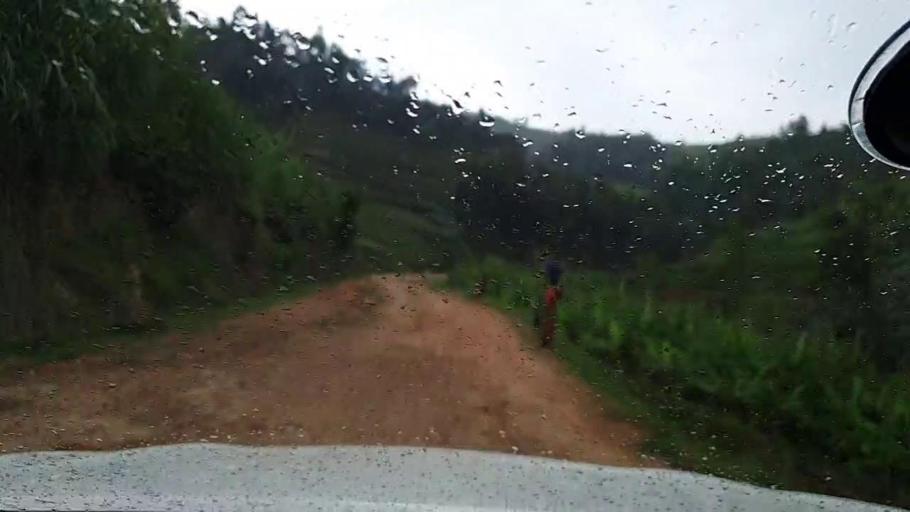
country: RW
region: Western Province
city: Kibuye
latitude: -2.0778
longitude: 29.4432
